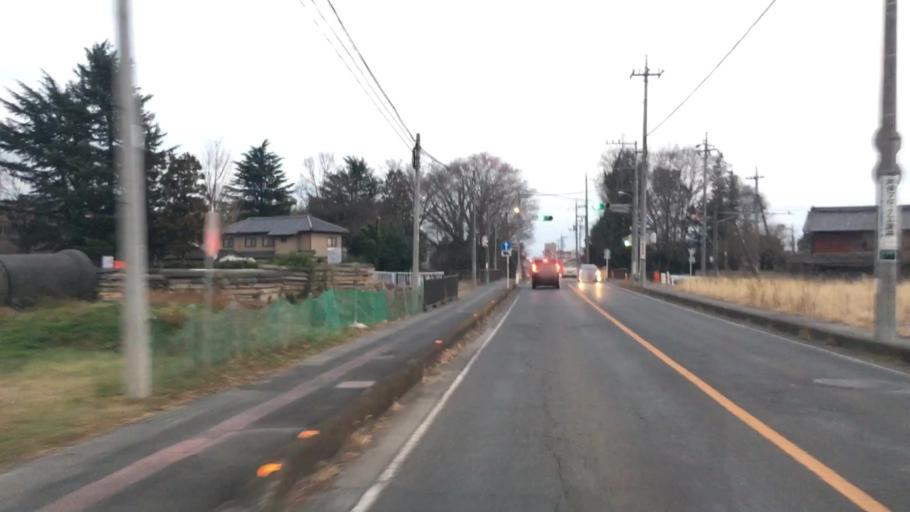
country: JP
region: Gunma
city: Ota
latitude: 36.3079
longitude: 139.3607
